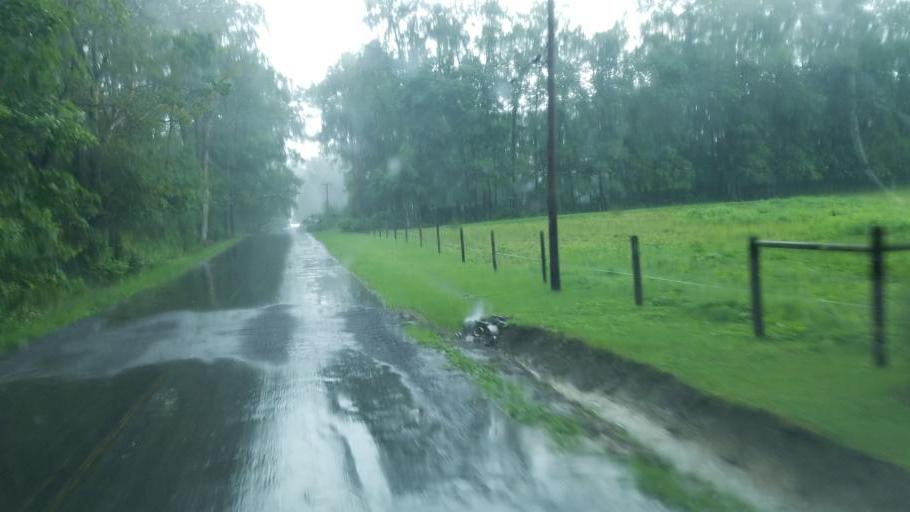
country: US
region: Ohio
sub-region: Geauga County
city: Middlefield
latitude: 41.4850
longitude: -80.9742
